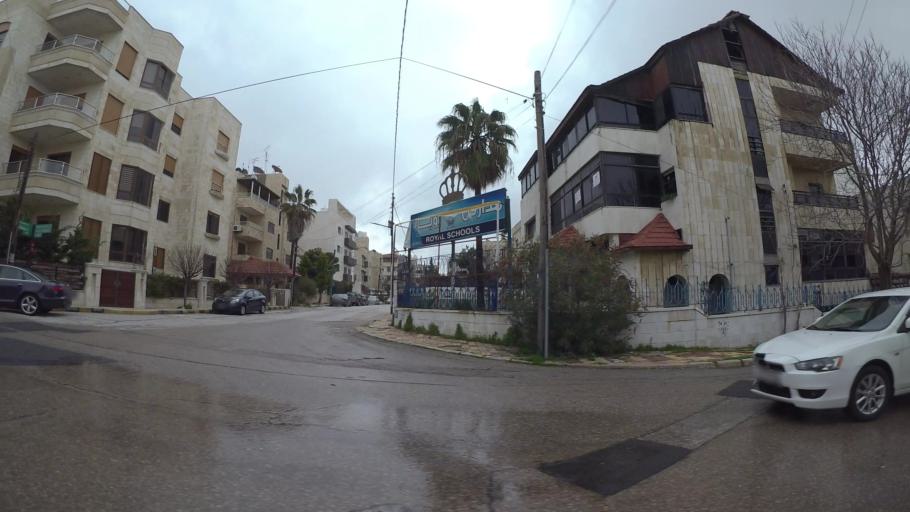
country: JO
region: Amman
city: Wadi as Sir
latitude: 31.9501
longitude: 35.8677
